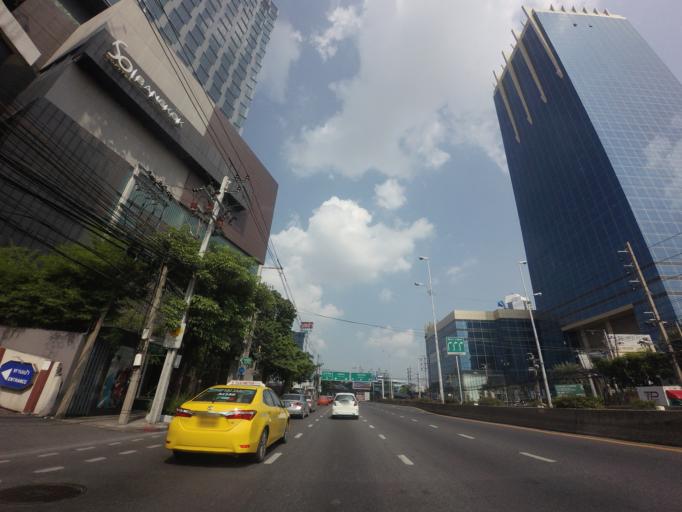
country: TH
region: Bangkok
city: Bang Rak
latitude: 13.7257
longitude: 100.5429
